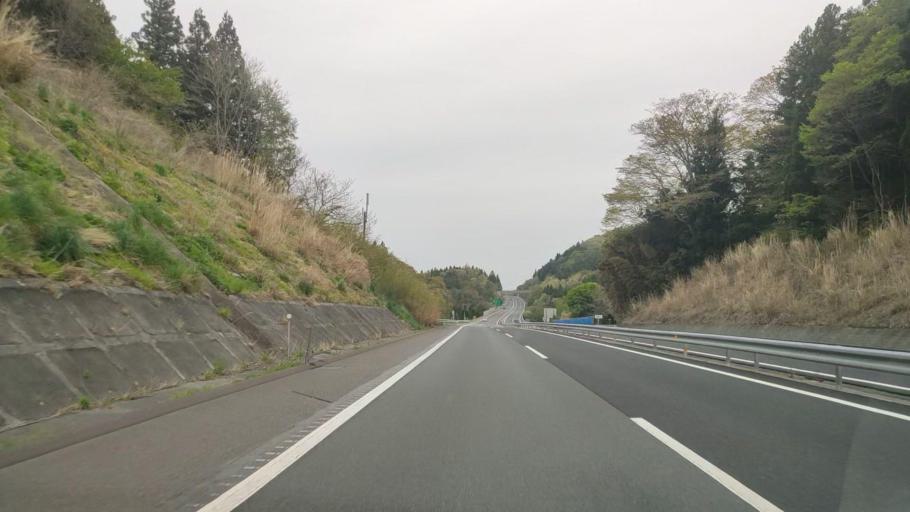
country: JP
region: Fukushima
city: Funehikimachi-funehiki
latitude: 37.2785
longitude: 140.6280
